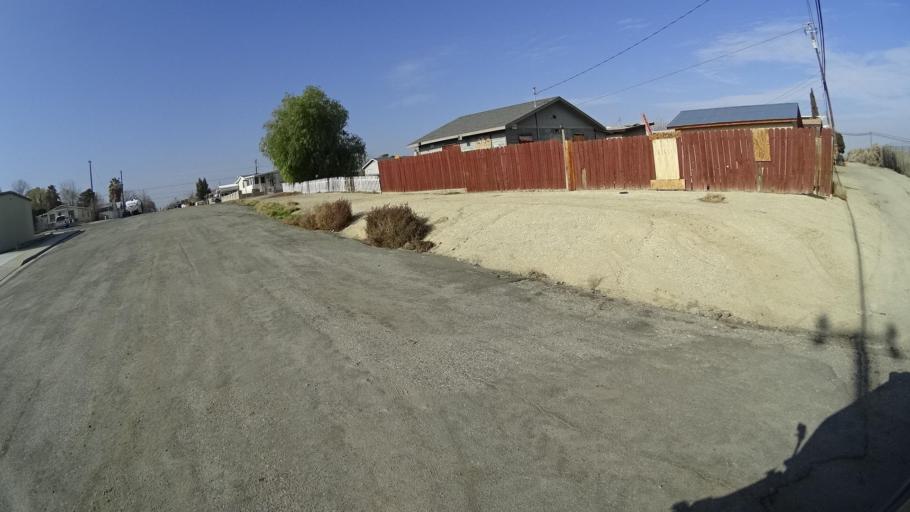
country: US
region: California
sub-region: Kern County
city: Ford City
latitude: 35.1576
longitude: -119.4518
